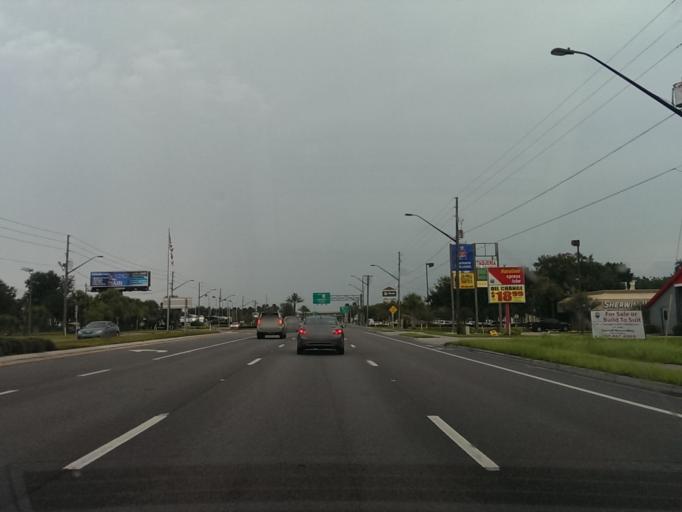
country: US
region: Florida
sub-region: Orange County
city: Winter Garden
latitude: 28.5512
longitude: -81.5639
